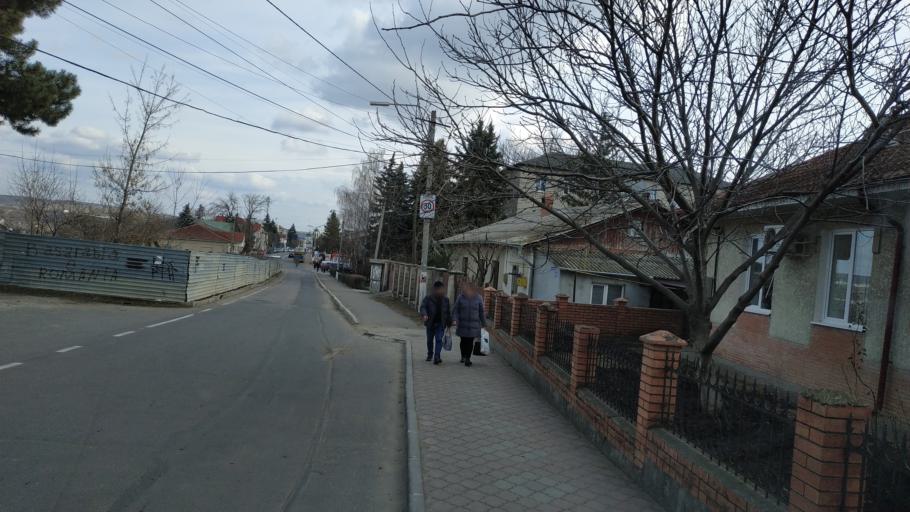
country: MD
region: Hincesti
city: Hincesti
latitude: 46.8289
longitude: 28.5873
